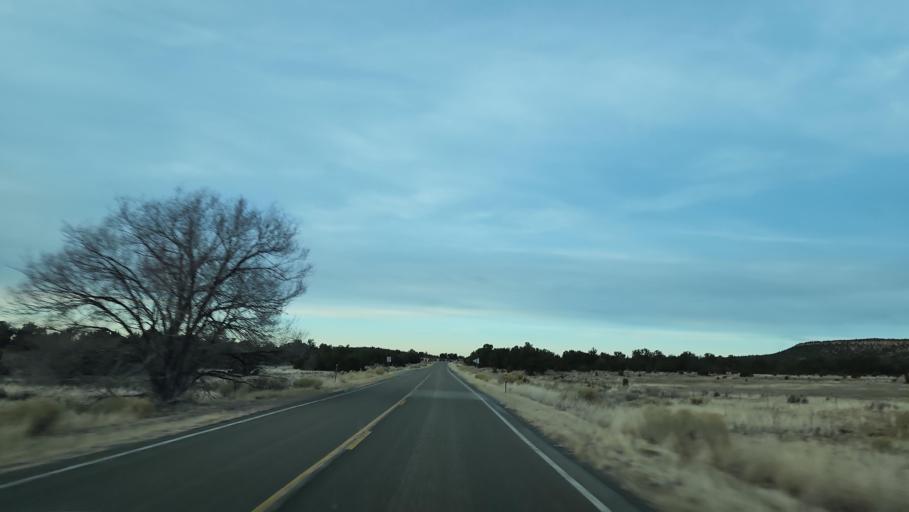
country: US
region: New Mexico
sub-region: Cibola County
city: Grants
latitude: 34.7352
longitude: -107.9652
